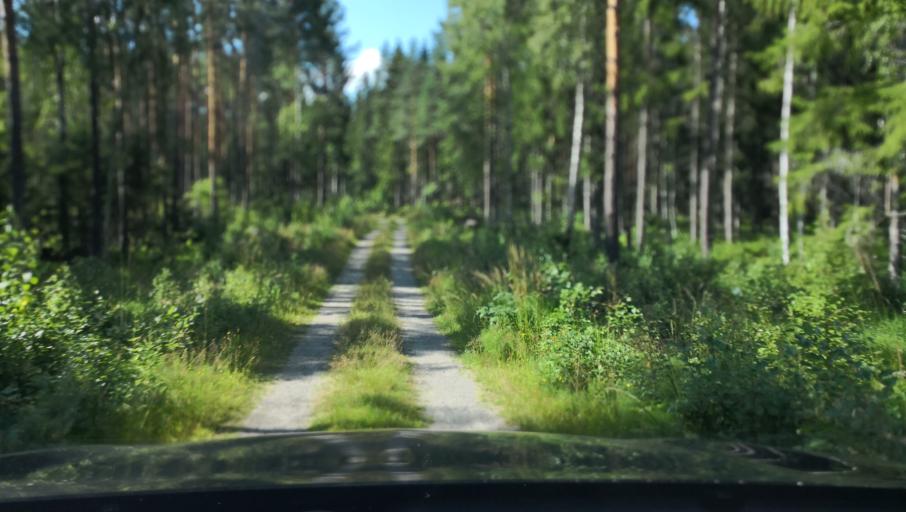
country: SE
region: Vaestmanland
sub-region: Vasteras
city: Skultuna
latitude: 59.7153
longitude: 16.3612
